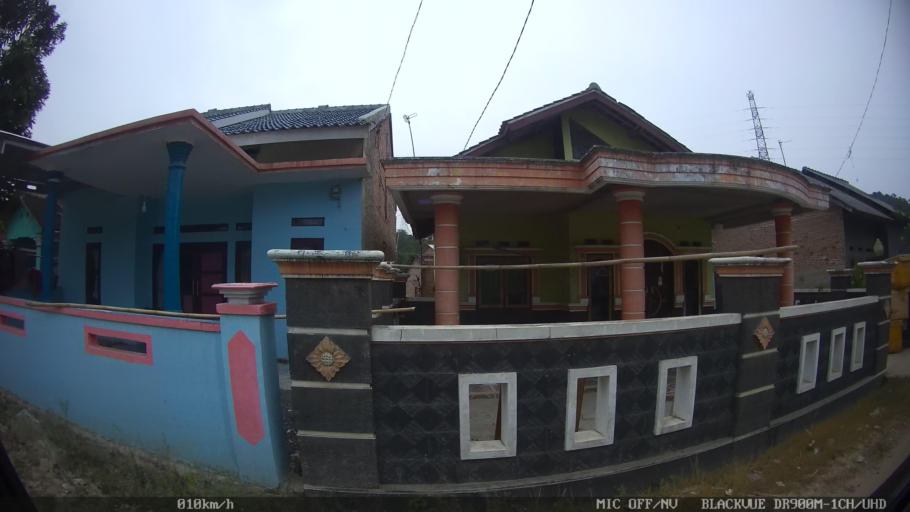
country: ID
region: Lampung
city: Panjang
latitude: -5.4253
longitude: 105.3437
